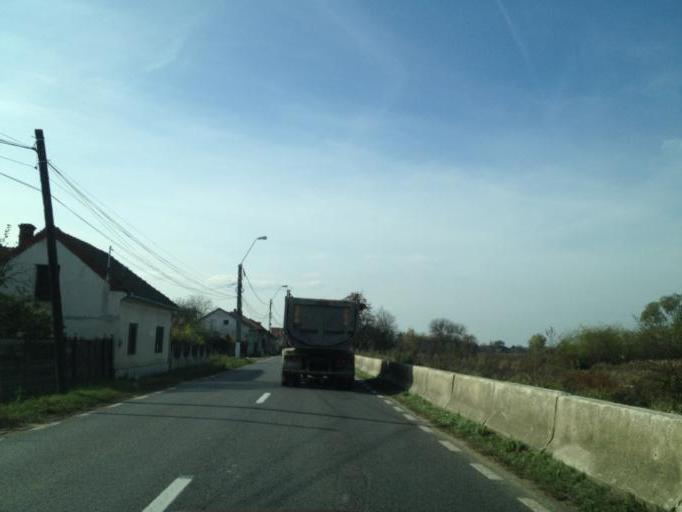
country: RO
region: Timis
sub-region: Comuna Faget
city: Faget
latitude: 45.8575
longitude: 22.1907
